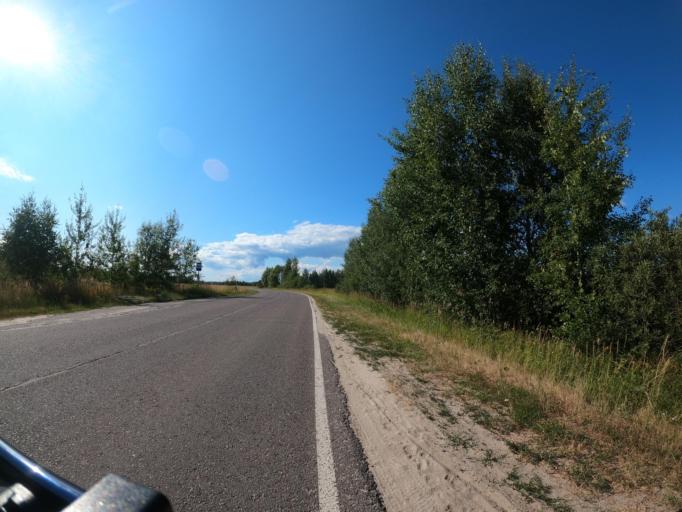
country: RU
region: Moskovskaya
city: Konobeyevo
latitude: 55.3978
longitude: 38.7160
